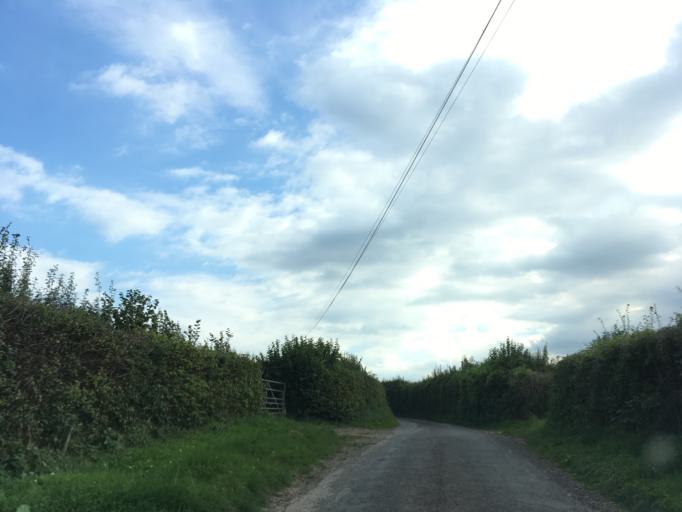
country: GB
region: England
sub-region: South Gloucestershire
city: Falfield
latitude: 51.6187
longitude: -2.4701
